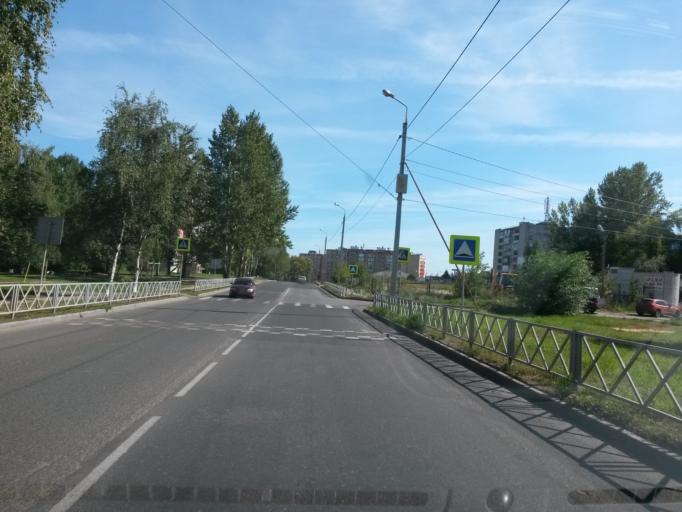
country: RU
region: Jaroslavl
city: Yaroslavl
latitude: 57.5801
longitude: 39.8569
